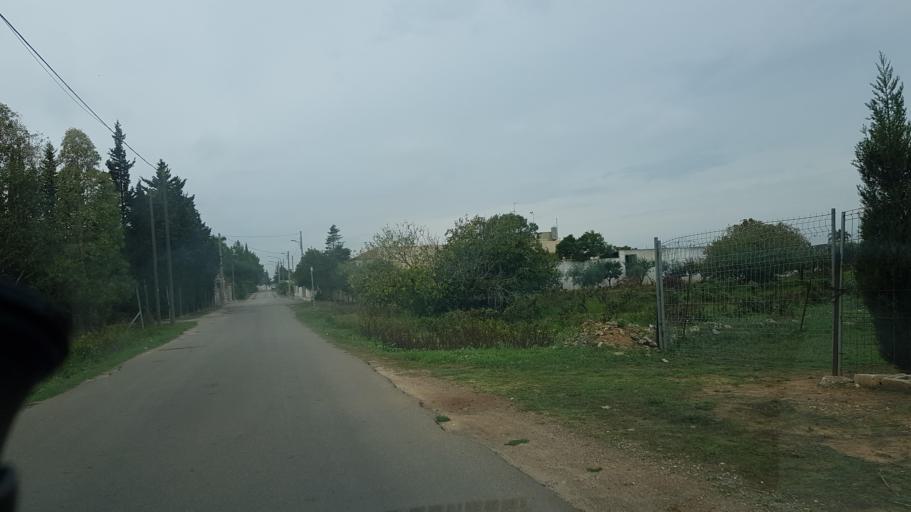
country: IT
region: Apulia
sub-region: Provincia di Brindisi
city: San Pietro Vernotico
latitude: 40.4820
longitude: 18.0128
